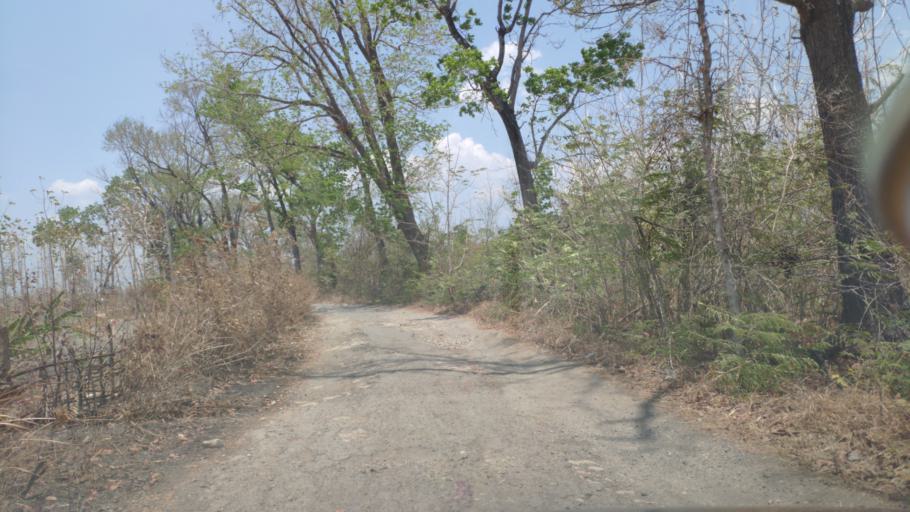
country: ID
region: Central Java
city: Randublatung
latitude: -7.2764
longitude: 111.3762
